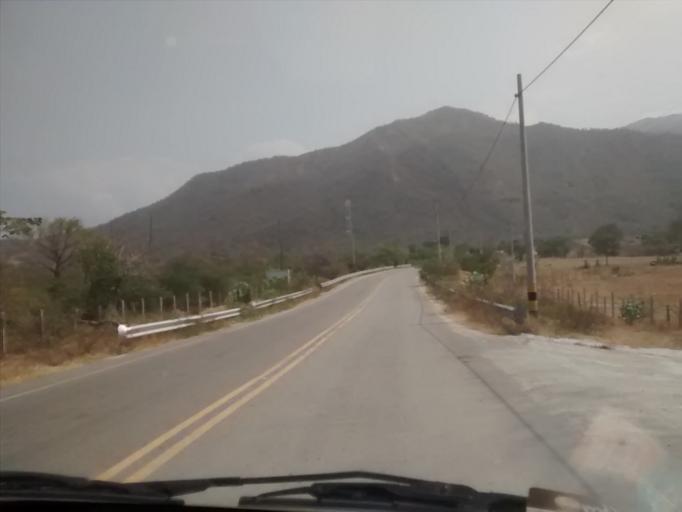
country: CO
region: Magdalena
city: Santa Marta
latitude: 11.1662
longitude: -74.2131
